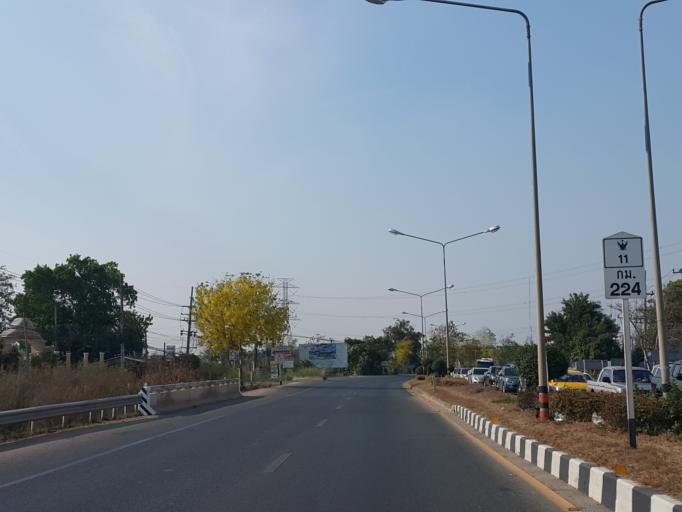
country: TH
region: Phitsanulok
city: Phitsanulok
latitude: 16.8200
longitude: 100.3309
